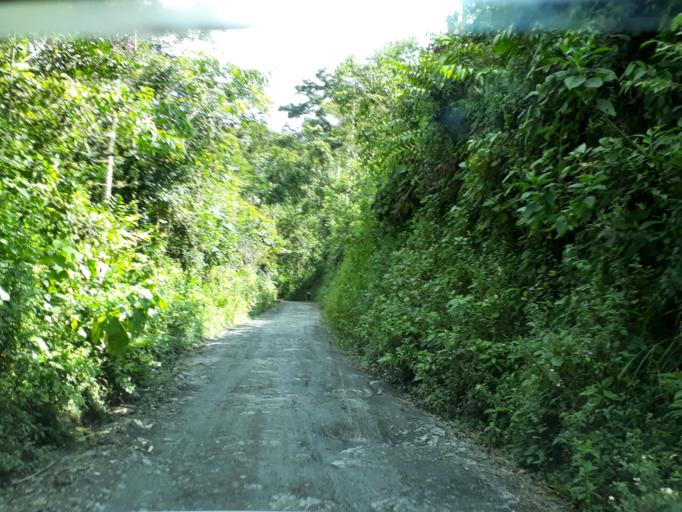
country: CO
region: Cundinamarca
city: Topaipi
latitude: 5.3945
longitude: -74.1988
